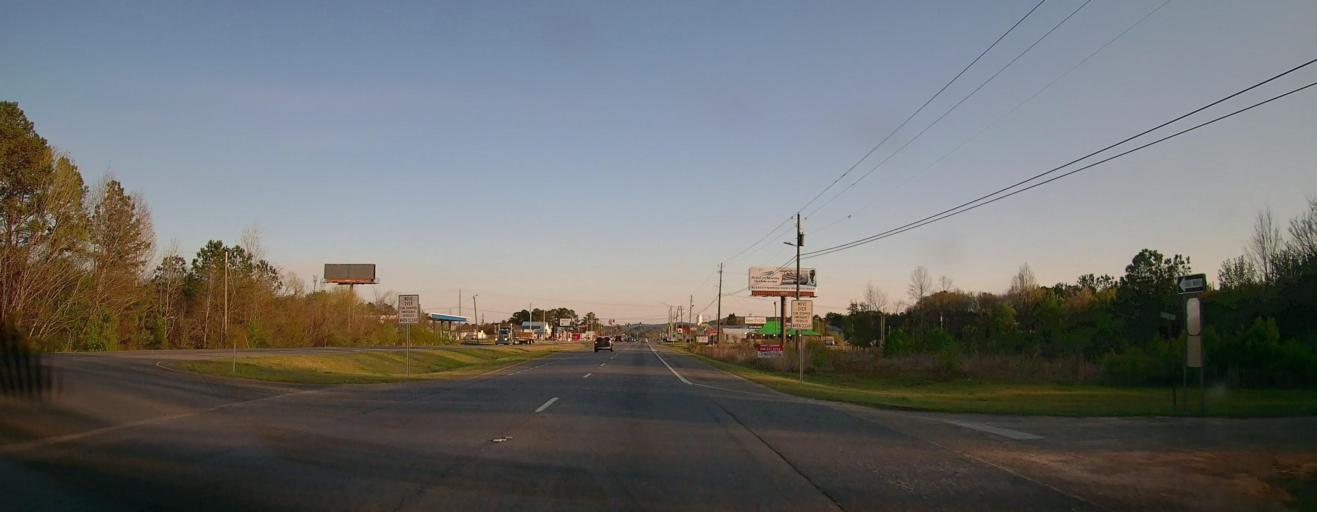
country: US
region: Alabama
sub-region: Talladega County
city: Childersburg
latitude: 33.2873
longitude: -86.3638
